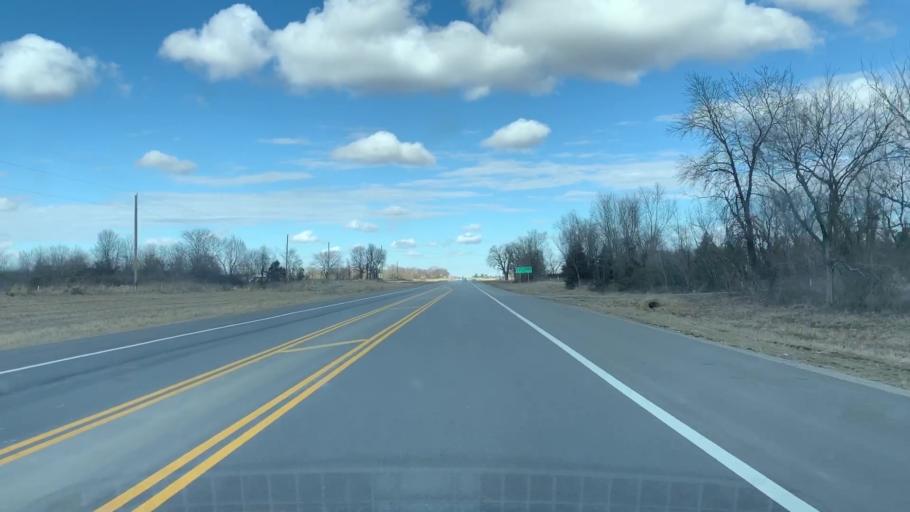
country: US
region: Kansas
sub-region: Cherokee County
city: Columbus
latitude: 37.2779
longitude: -94.8321
